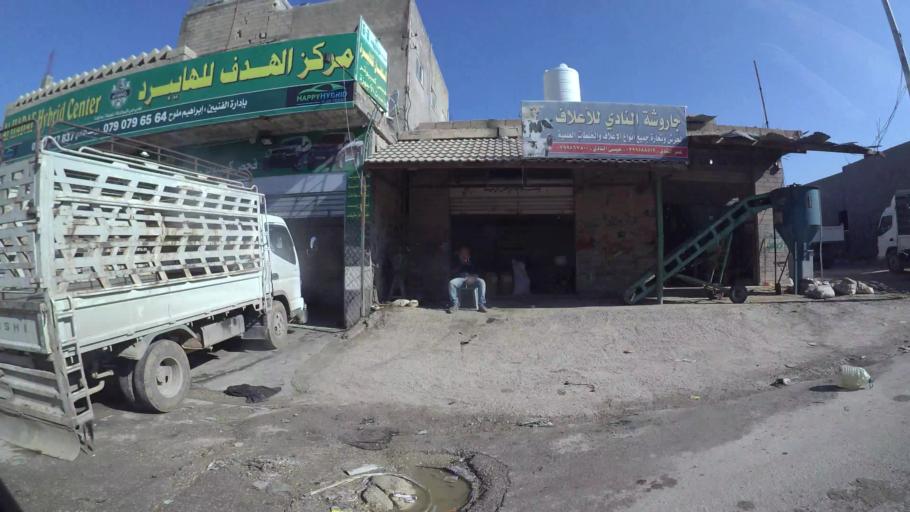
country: JO
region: Amman
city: Al Jubayhah
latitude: 32.0801
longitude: 35.8491
